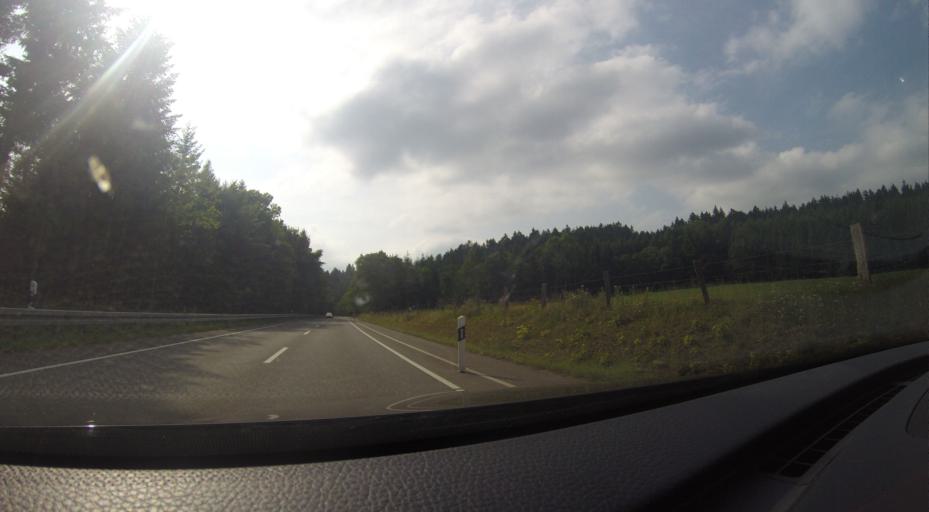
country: DE
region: North Rhine-Westphalia
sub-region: Regierungsbezirk Arnsberg
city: Medebach
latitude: 51.2130
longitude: 8.6548
